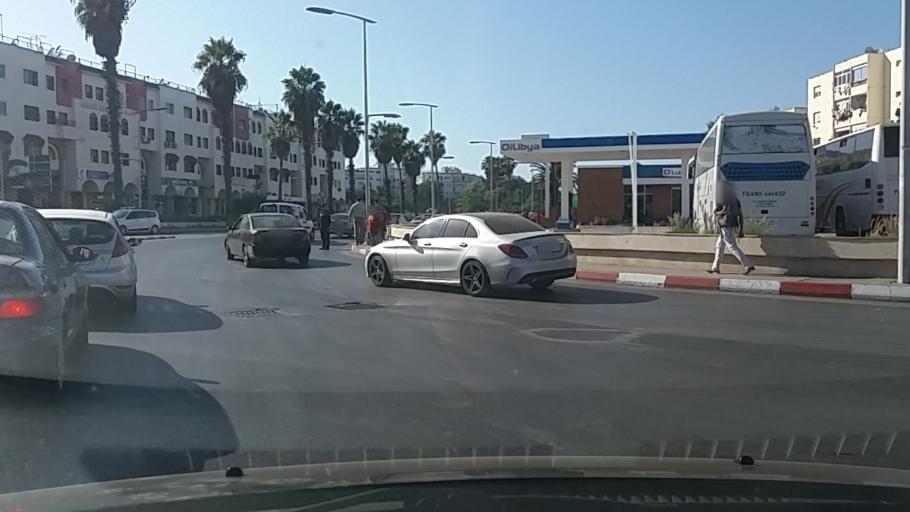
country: MA
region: Rabat-Sale-Zemmour-Zaer
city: Sale
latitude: 34.0407
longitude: -6.8159
